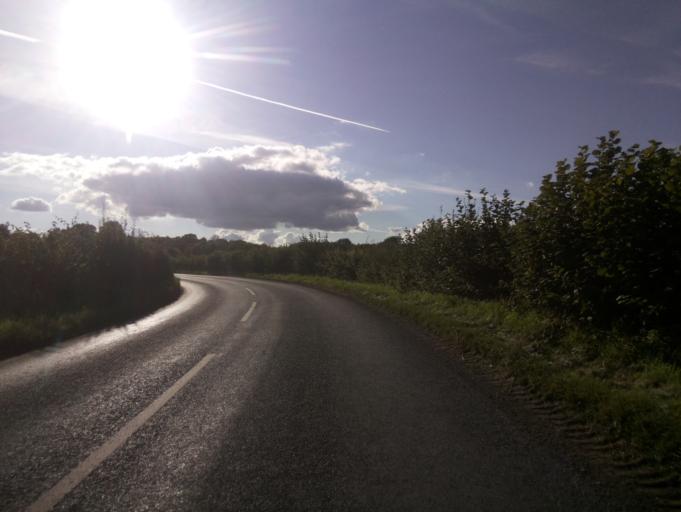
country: GB
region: England
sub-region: Herefordshire
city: Clifford
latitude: 52.1134
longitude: -3.0951
